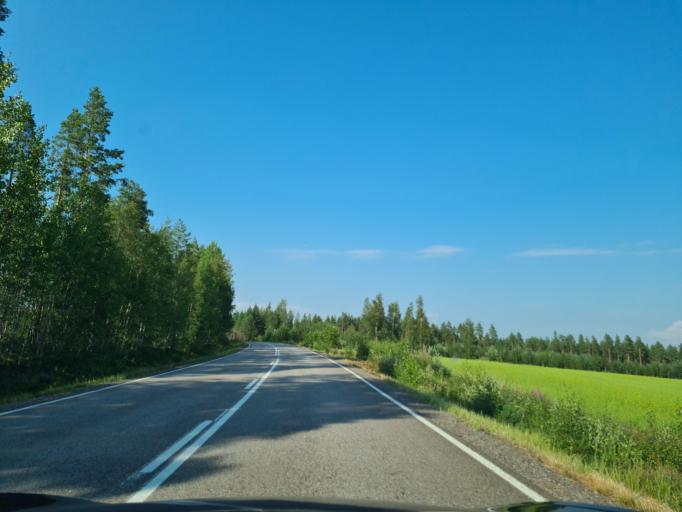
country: FI
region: Satakunta
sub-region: Pohjois-Satakunta
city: Karvia
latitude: 62.3119
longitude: 22.6548
